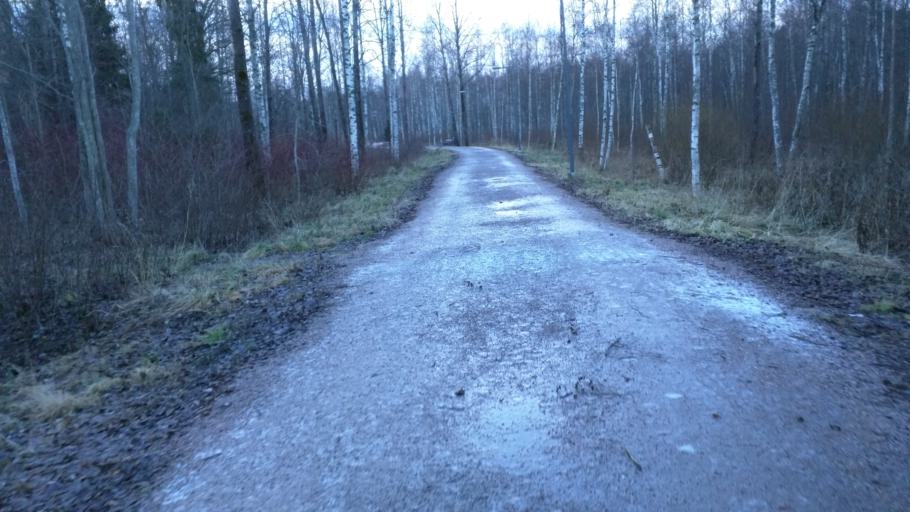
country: FI
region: Uusimaa
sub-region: Helsinki
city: Kauniainen
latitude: 60.2405
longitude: 24.7337
